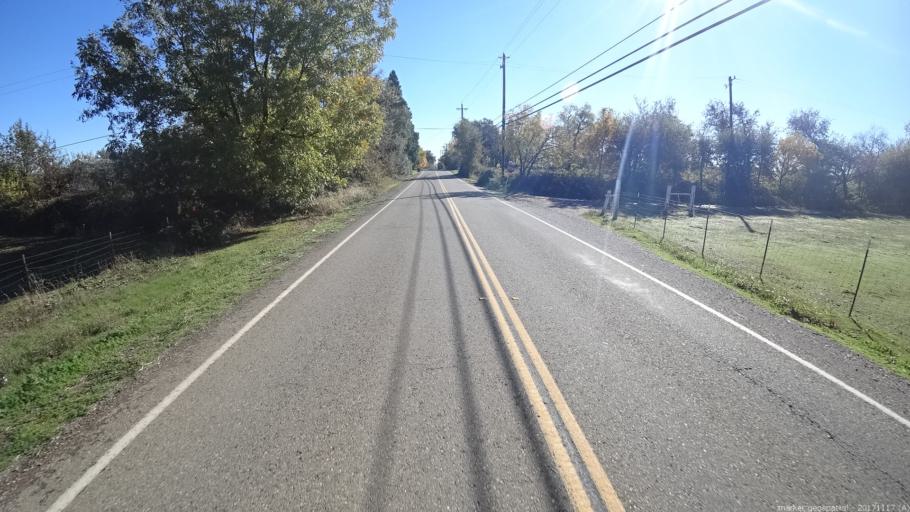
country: US
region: California
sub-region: Shasta County
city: Cottonwood
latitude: 40.4288
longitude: -122.2289
